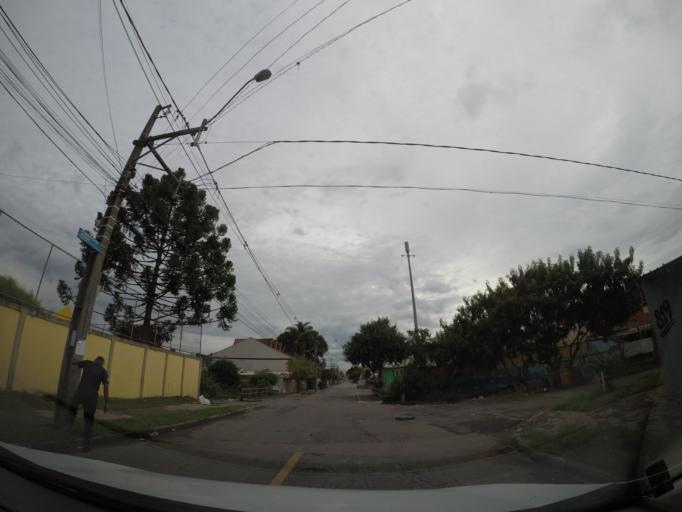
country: BR
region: Parana
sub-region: Curitiba
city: Curitiba
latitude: -25.4495
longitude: -49.2471
